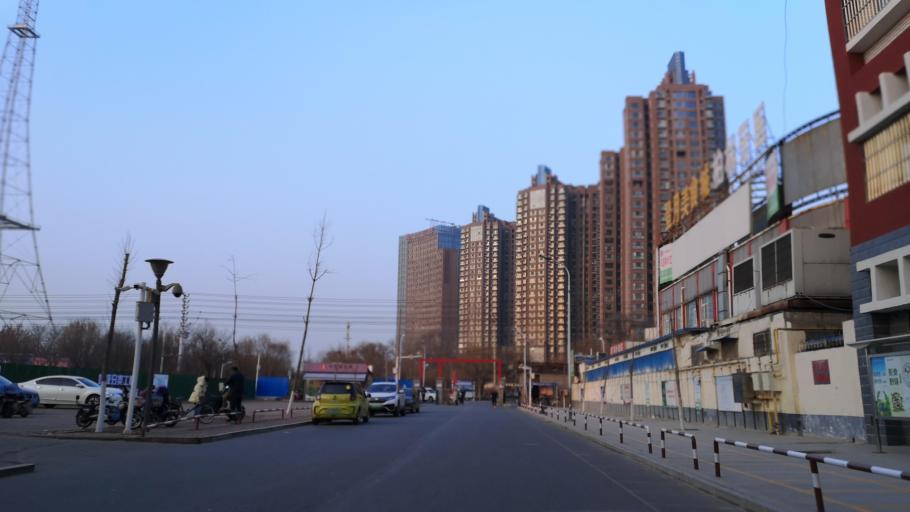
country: CN
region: Henan Sheng
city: Zhongyuanlu
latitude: 35.7708
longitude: 115.0791
